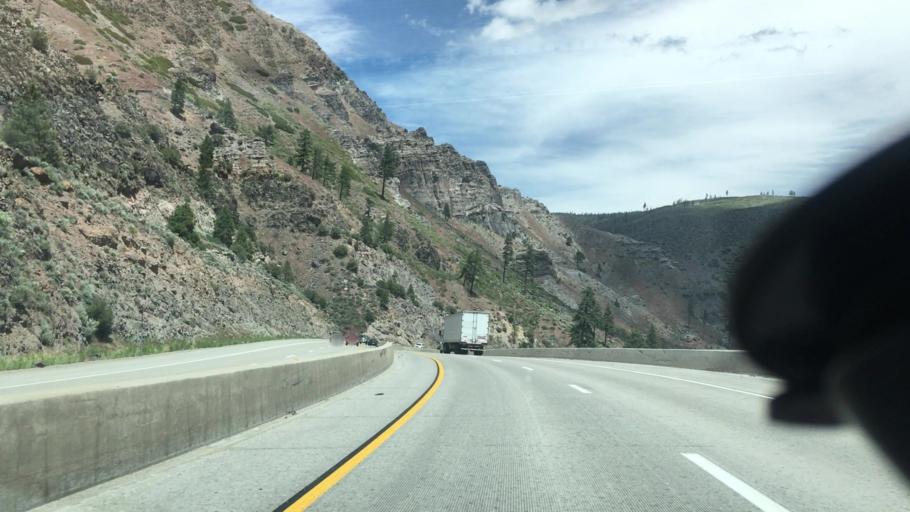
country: US
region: California
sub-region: Placer County
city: Tahoe Vista
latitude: 39.3739
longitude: -120.0323
